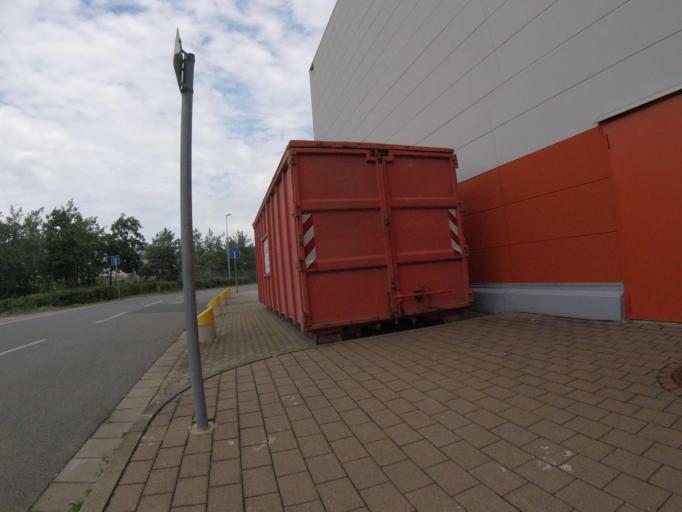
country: DE
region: Brandenburg
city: Wildau
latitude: 52.3153
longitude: 13.6059
